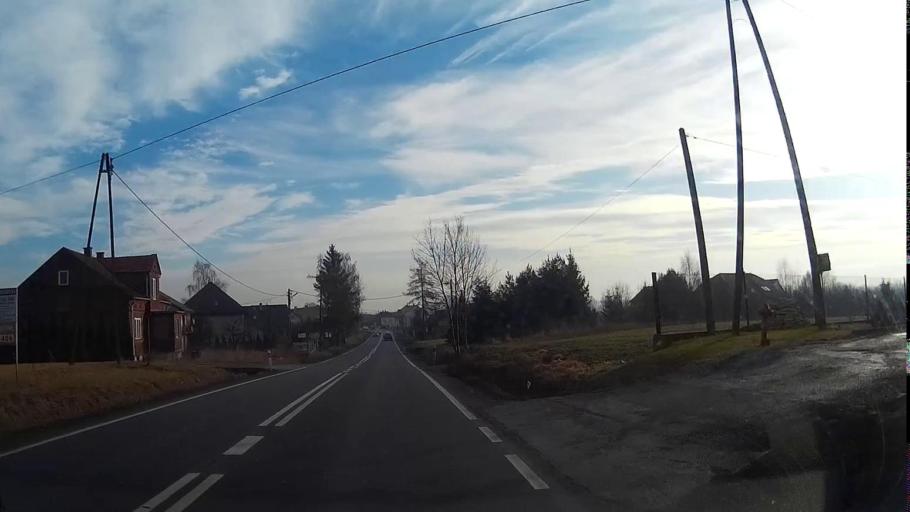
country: PL
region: Lesser Poland Voivodeship
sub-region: Powiat krakowski
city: Kaszow
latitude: 50.0387
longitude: 19.7092
